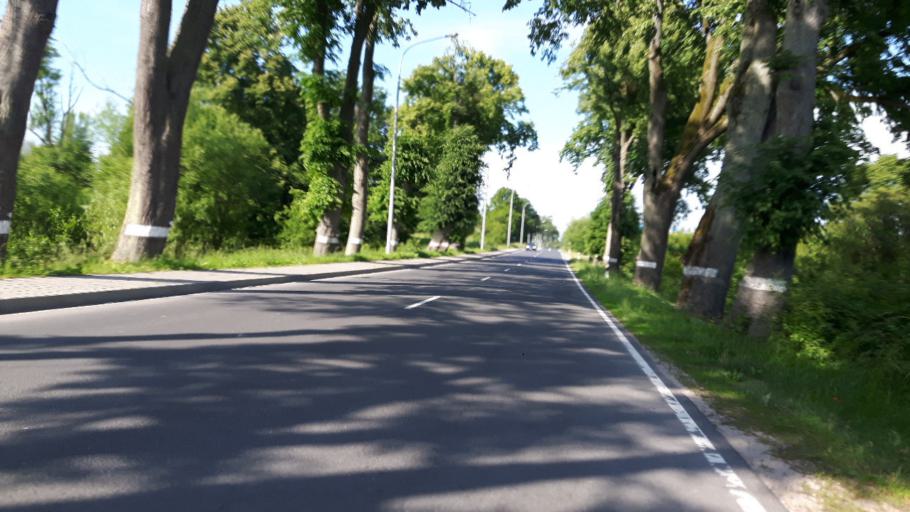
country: RU
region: Kaliningrad
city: Mamonovo
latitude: 54.4550
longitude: 19.9231
